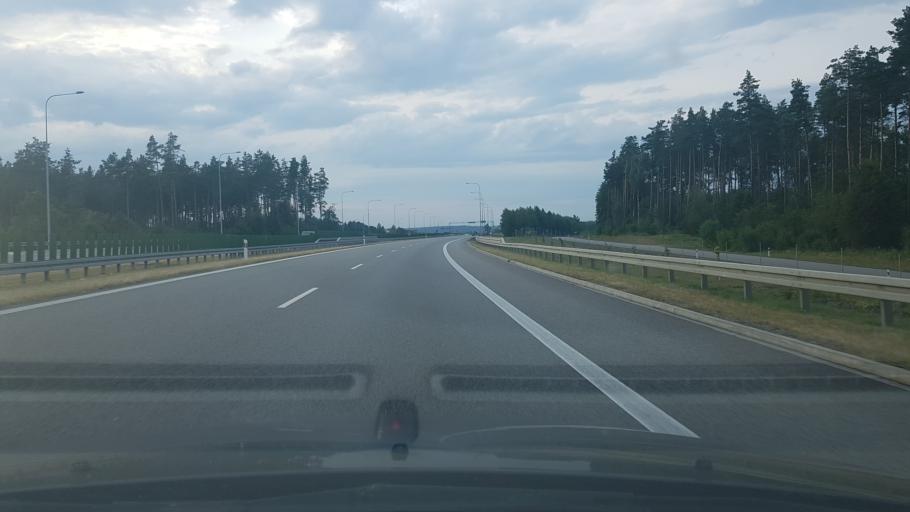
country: PL
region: Warmian-Masurian Voivodeship
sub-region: Powiat ostrodzki
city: Milomlyn
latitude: 53.7624
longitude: 19.8556
